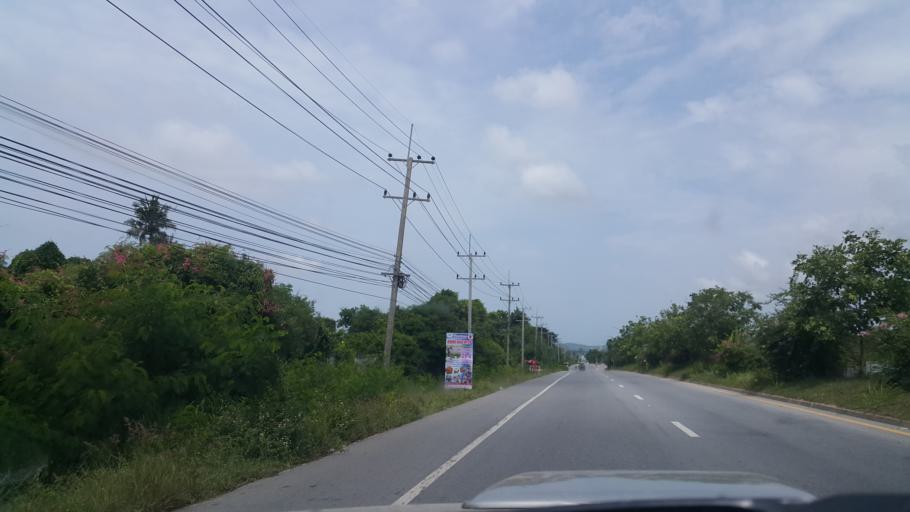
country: TH
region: Rayong
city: Ban Chang
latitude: 12.7078
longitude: 101.0230
